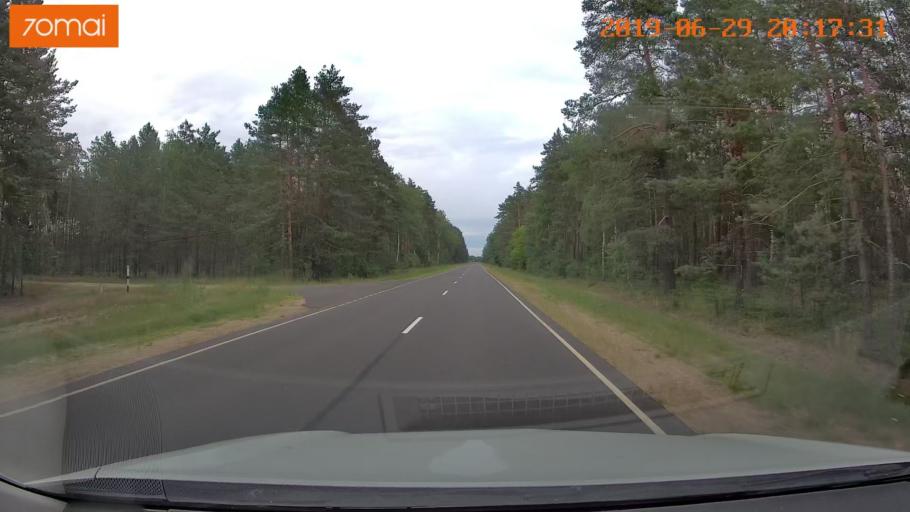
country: BY
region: Brest
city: Asnyezhytsy
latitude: 52.3886
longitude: 26.2180
